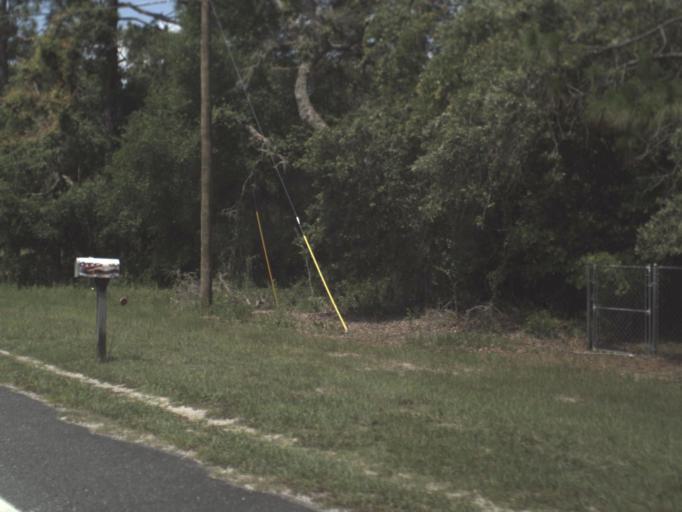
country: US
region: Florida
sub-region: Levy County
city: Williston Highlands
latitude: 29.2940
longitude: -82.5335
